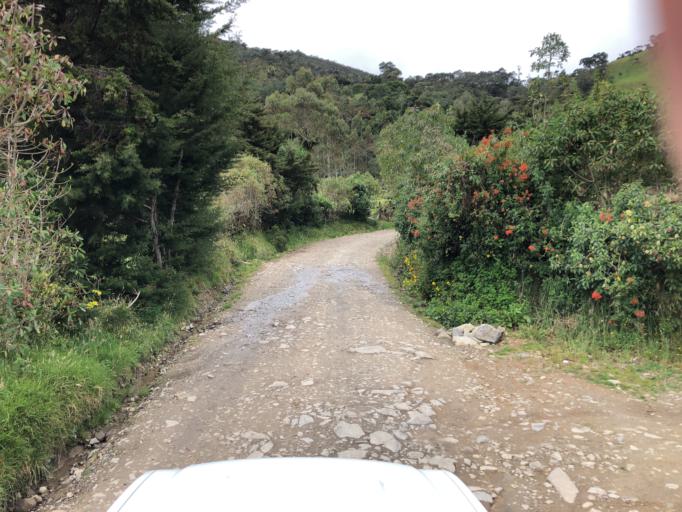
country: CO
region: Cauca
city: Totoro
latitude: 2.5023
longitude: -76.3583
